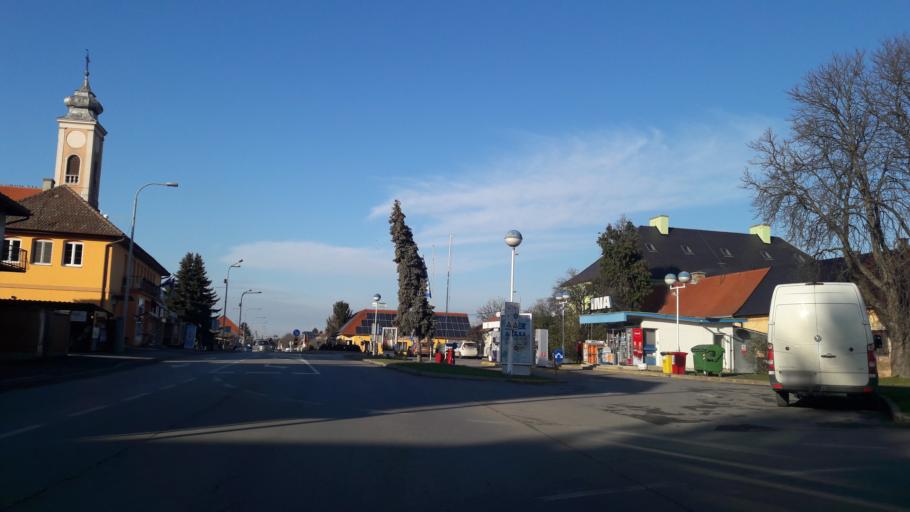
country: HR
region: Osjecko-Baranjska
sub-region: Grad Osijek
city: Bilje
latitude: 45.6031
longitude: 18.7440
